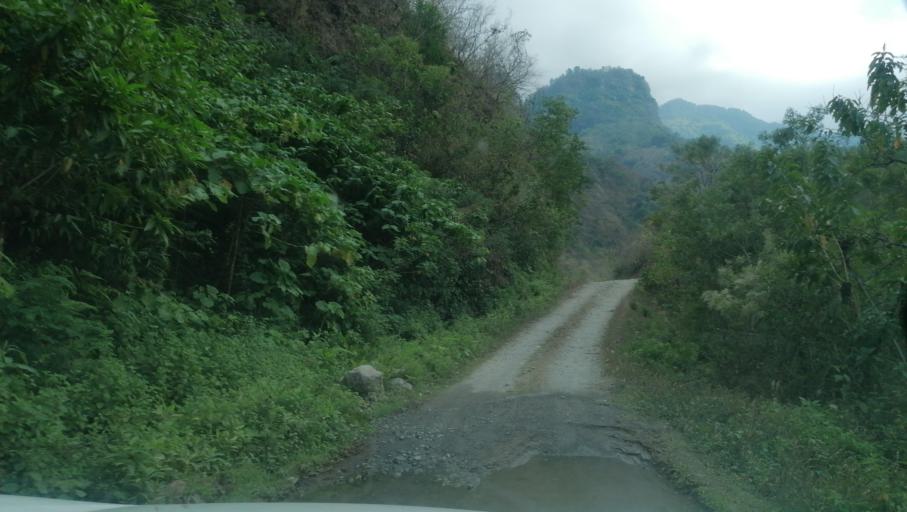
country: MX
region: Chiapas
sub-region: Cacahoatan
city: Benito Juarez
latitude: 15.1640
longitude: -92.1793
